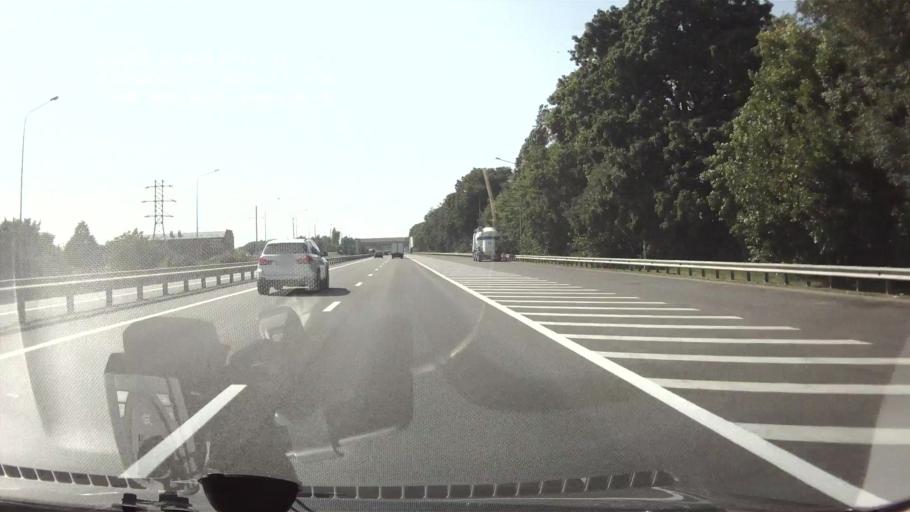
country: RU
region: Krasnodarskiy
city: Pashkovskiy
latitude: 45.0241
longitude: 39.2108
